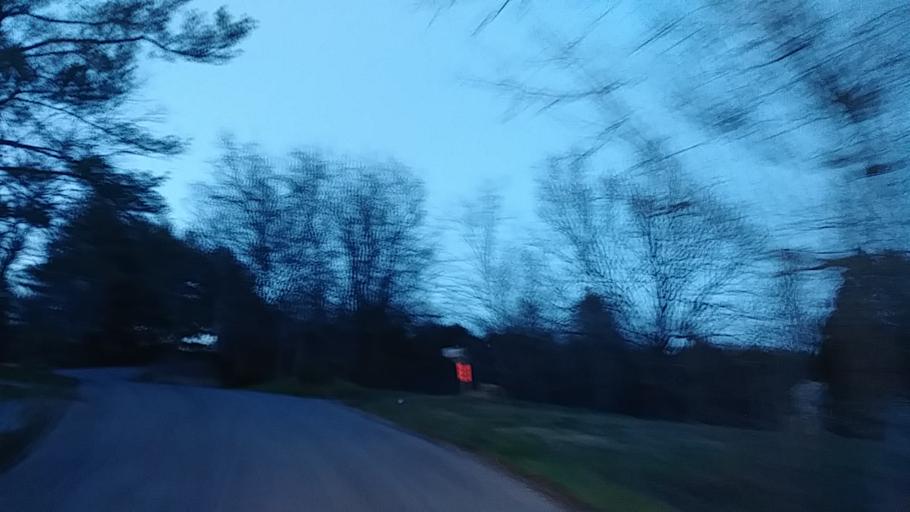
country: US
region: Tennessee
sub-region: Greene County
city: Mosheim
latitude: 36.0646
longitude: -82.9869
